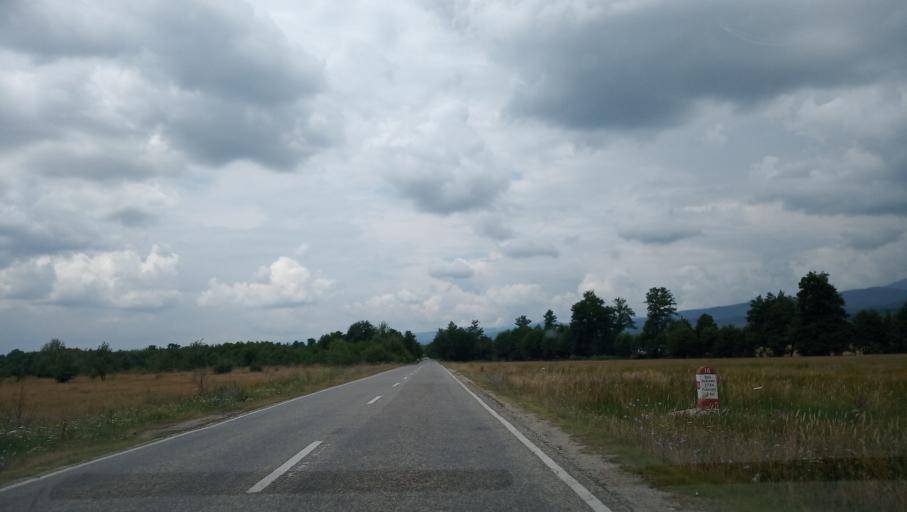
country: RO
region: Gorj
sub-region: Comuna Runcu
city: Valea Mare
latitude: 45.0866
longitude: 23.0842
